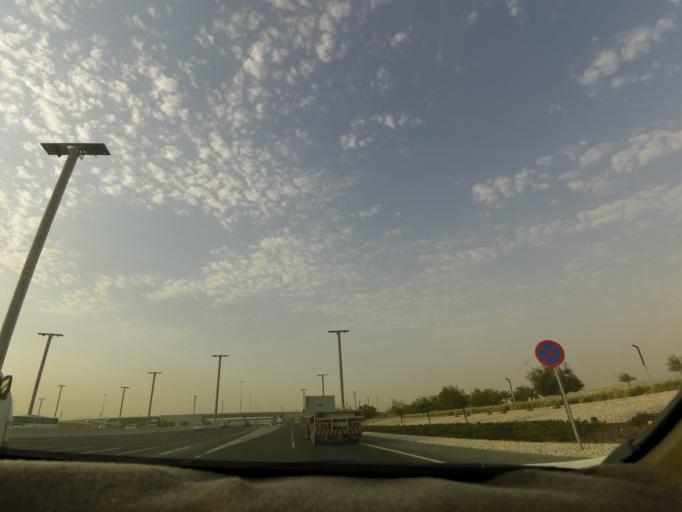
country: QA
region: Al Wakrah
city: Al Wakrah
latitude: 25.2447
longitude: 51.5891
